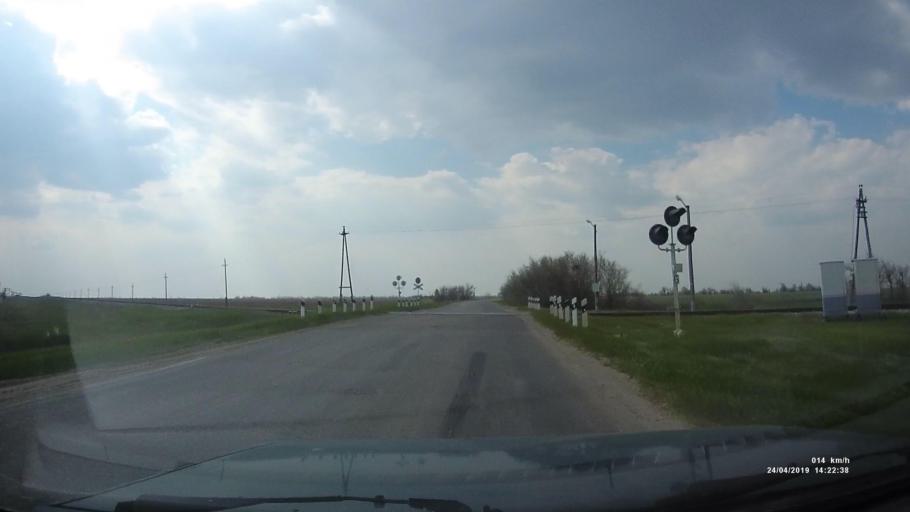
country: RU
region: Kalmykiya
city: Arshan'
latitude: 46.3174
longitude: 44.1226
